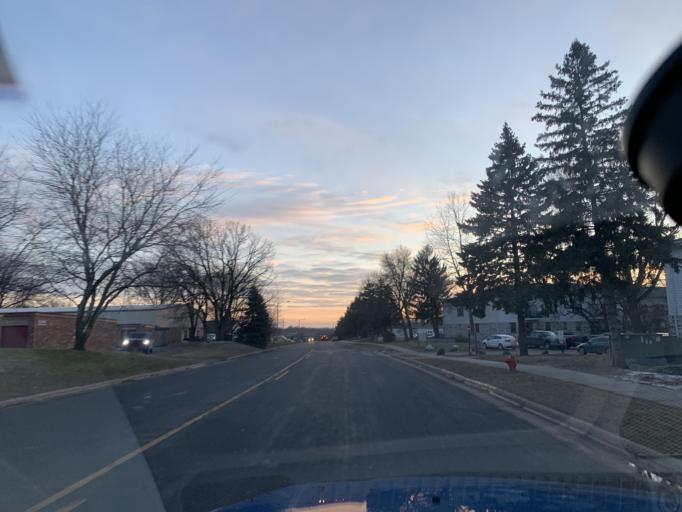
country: US
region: Wisconsin
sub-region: Dane County
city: Shorewood Hills
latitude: 43.0233
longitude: -89.4714
